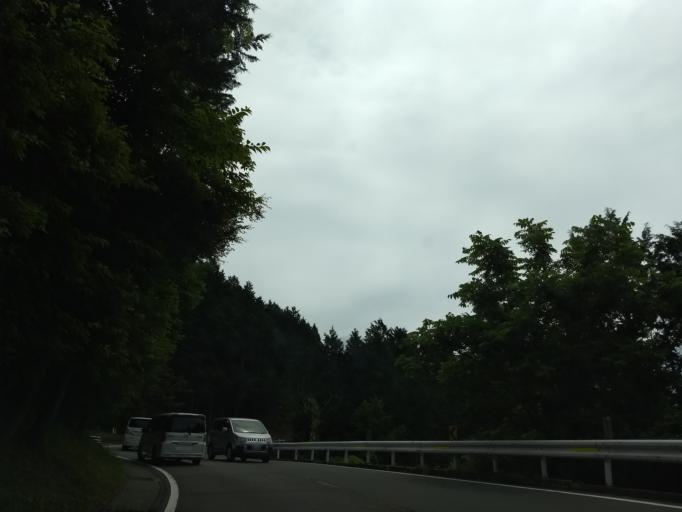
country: JP
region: Shizuoka
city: Gotemba
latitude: 35.3832
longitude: 138.8542
